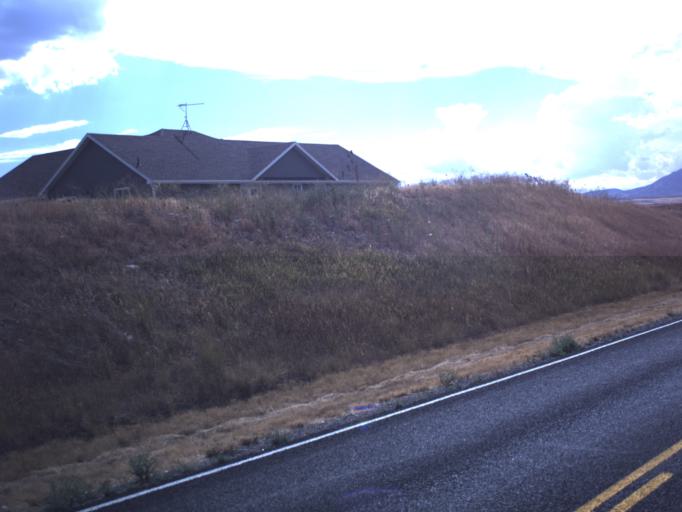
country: US
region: Utah
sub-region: Cache County
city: Richmond
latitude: 41.9236
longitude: -111.8418
